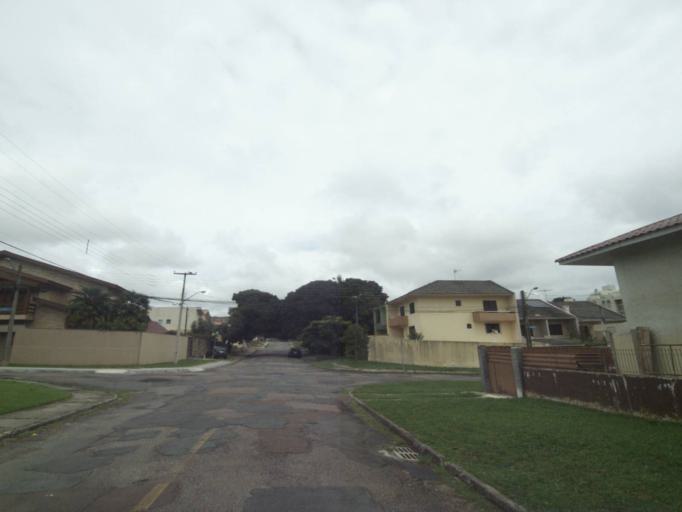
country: BR
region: Parana
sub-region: Curitiba
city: Curitiba
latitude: -25.4815
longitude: -49.2849
